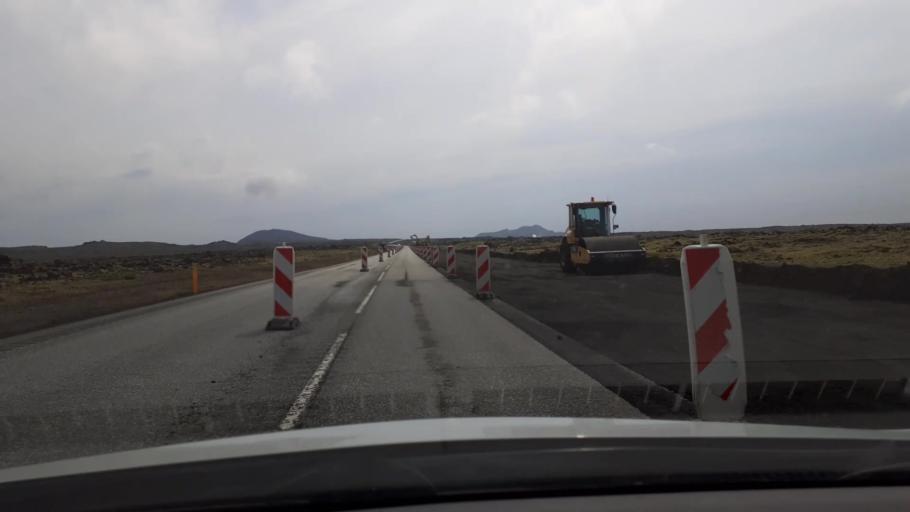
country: IS
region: Southern Peninsula
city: Vogar
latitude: 63.9197
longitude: -22.4216
